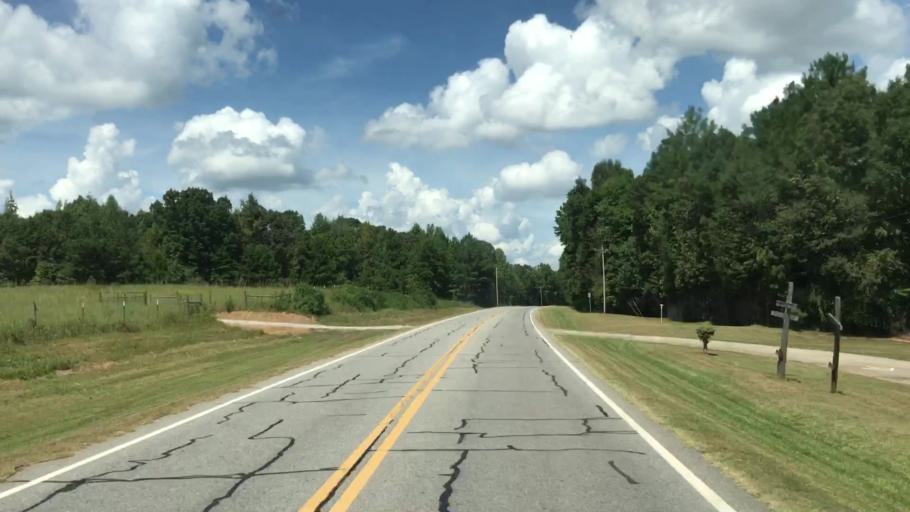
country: US
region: Georgia
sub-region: Oconee County
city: Watkinsville
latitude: 33.7572
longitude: -83.3063
